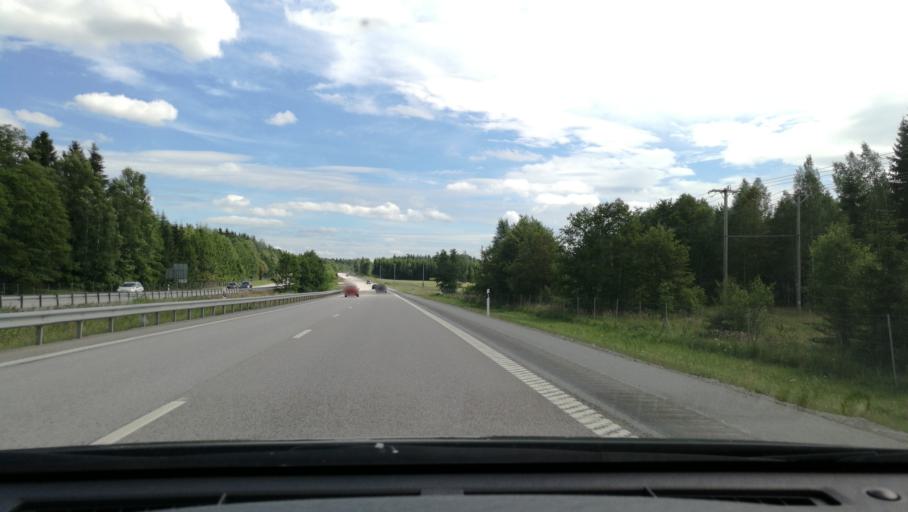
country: SE
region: Uppsala
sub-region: Habo Kommun
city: Balsta
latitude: 59.5575
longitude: 17.5784
